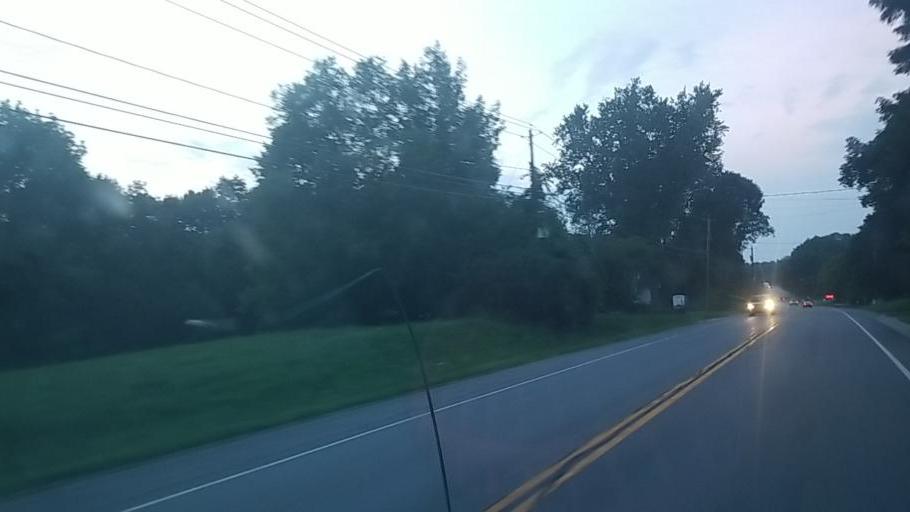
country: US
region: New York
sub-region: Montgomery County
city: Fonda
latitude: 42.9641
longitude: -74.3873
